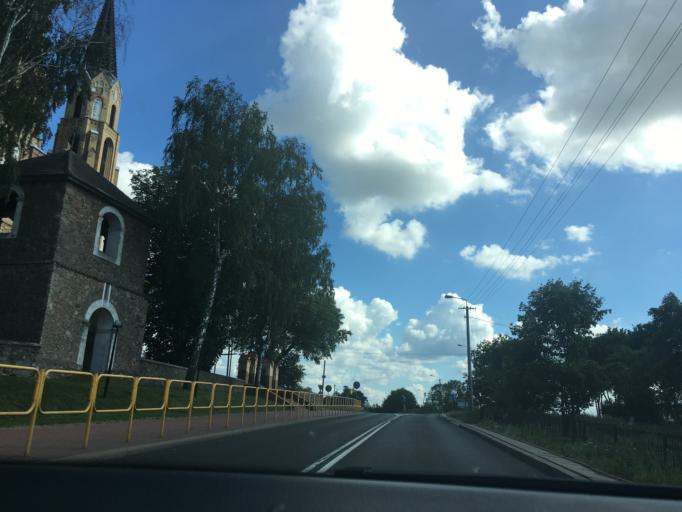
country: PL
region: Podlasie
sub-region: Powiat sokolski
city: Suchowola
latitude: 53.4414
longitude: 23.0952
